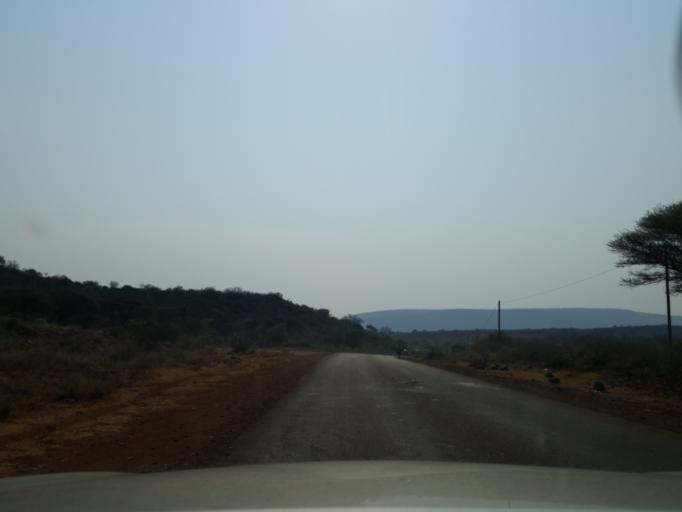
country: BW
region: South East
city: Lobatse
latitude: -25.3044
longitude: 25.8219
